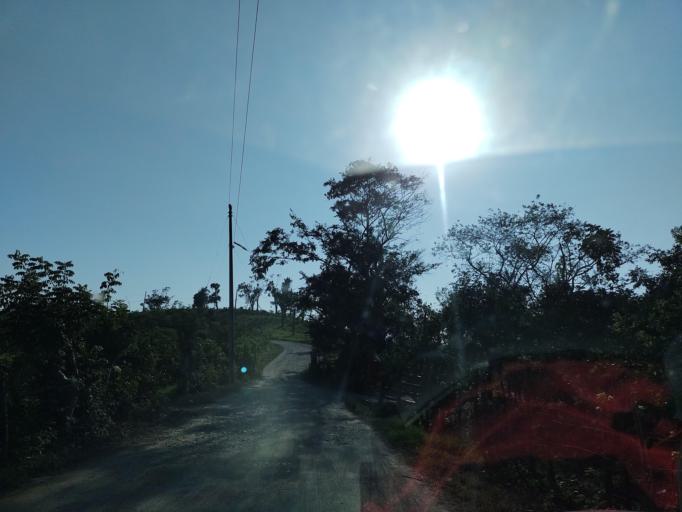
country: MX
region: Veracruz
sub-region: Papantla
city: Polutla
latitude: 20.4571
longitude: -97.2402
